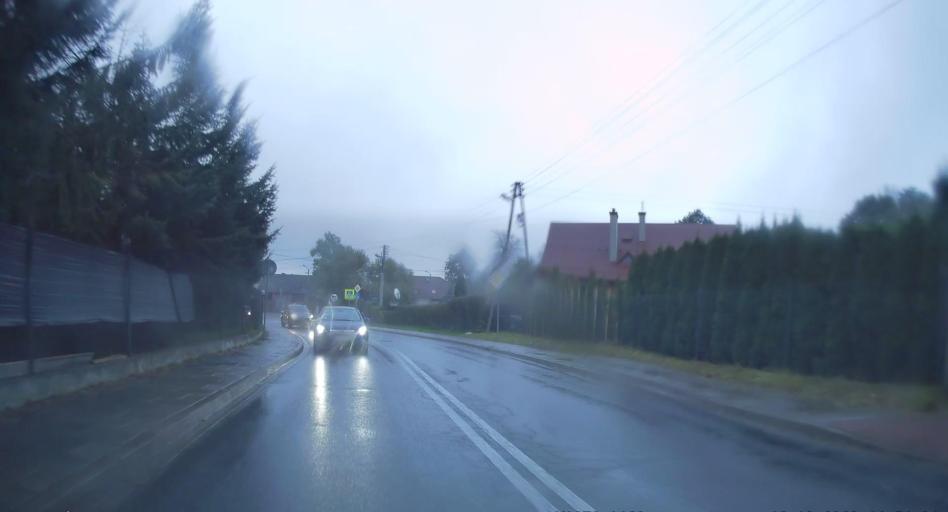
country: PL
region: Lesser Poland Voivodeship
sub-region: Powiat krakowski
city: Ochojno
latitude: 49.9793
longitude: 19.9891
